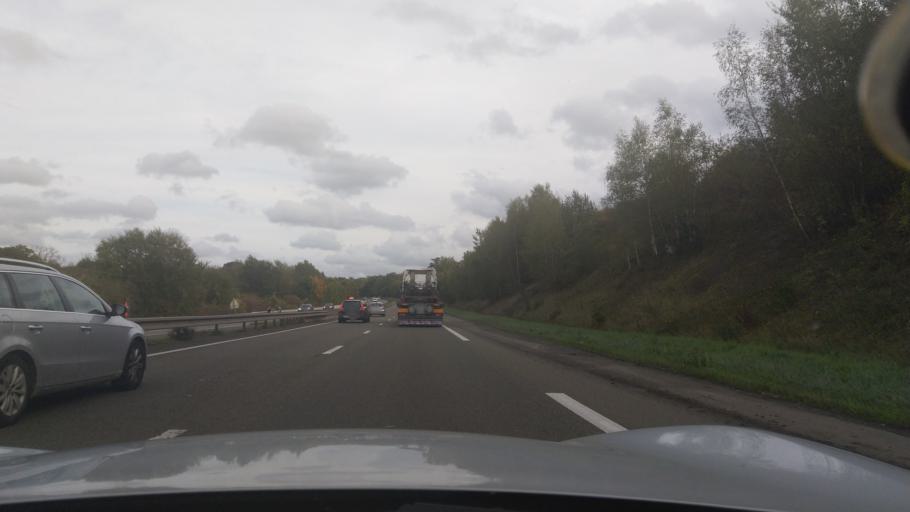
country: FR
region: Ile-de-France
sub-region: Departement du Val-d'Oise
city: Meriel
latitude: 49.0715
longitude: 2.2447
